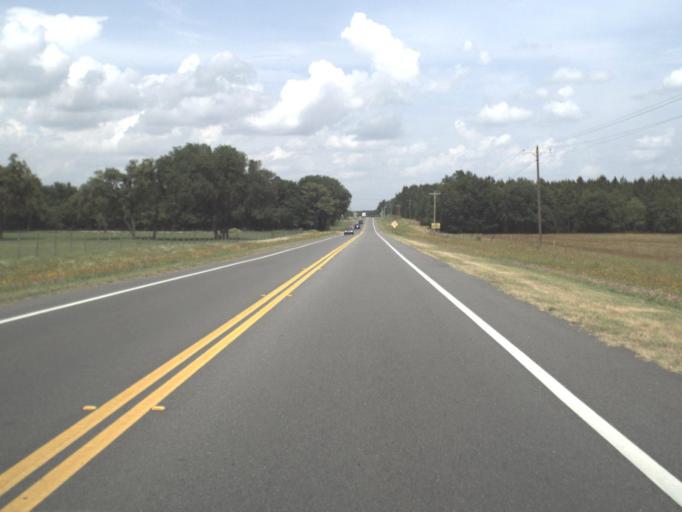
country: US
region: Florida
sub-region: Alachua County
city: Hawthorne
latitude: 29.6053
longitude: -82.0346
